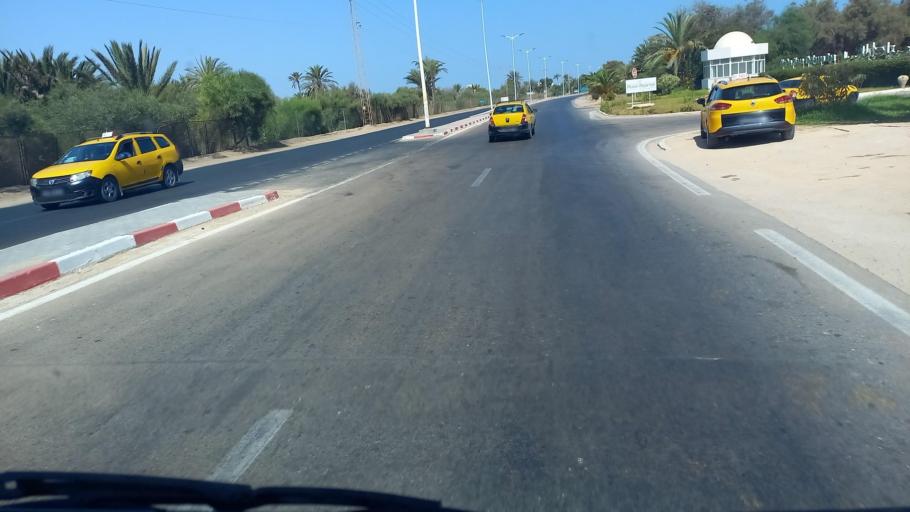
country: TN
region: Madanin
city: Midoun
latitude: 33.8300
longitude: 11.0075
